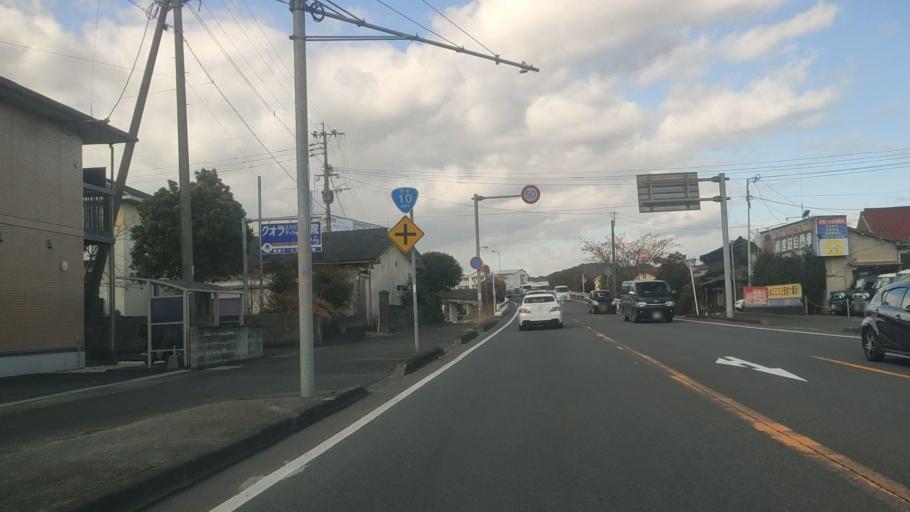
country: JP
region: Kagoshima
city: Kajiki
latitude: 31.7346
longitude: 130.6541
